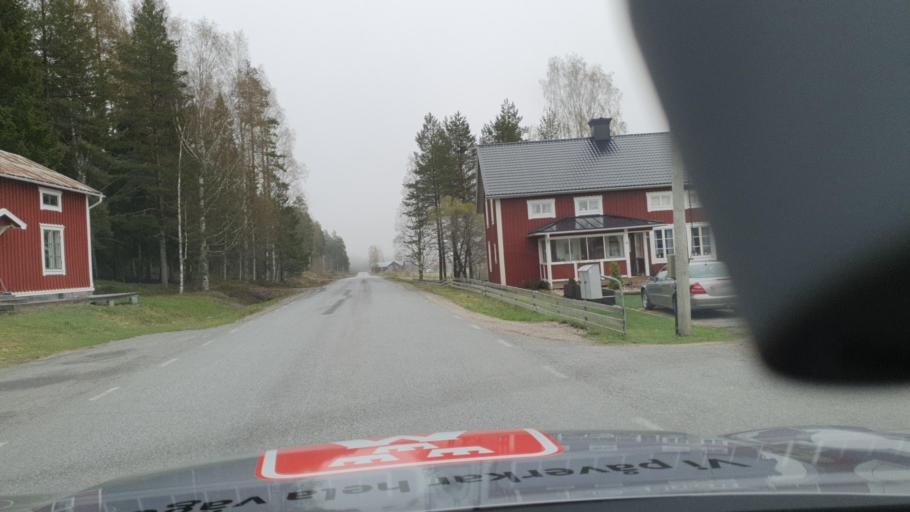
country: SE
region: Vaesternorrland
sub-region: OErnskoeldsviks Kommun
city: Husum
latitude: 63.5329
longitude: 19.1119
